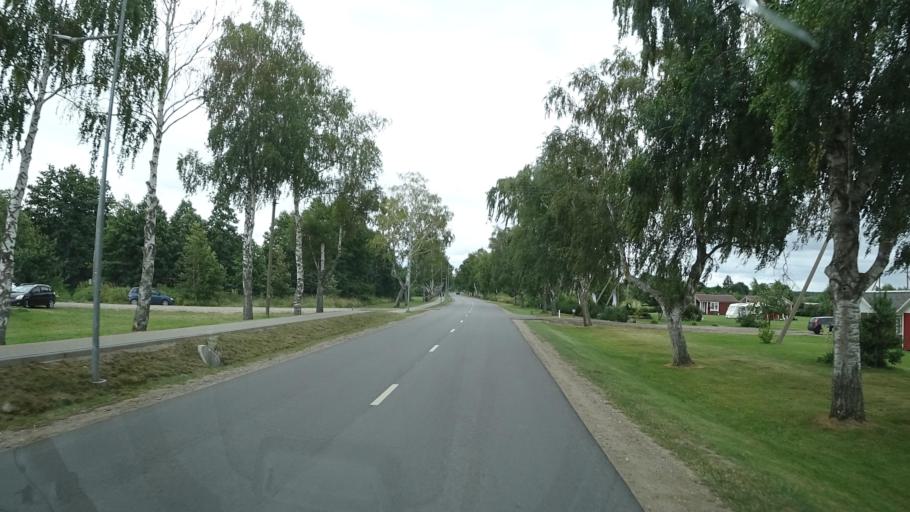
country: LT
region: Klaipedos apskritis
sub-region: Palanga
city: Sventoji
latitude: 56.0295
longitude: 21.0891
